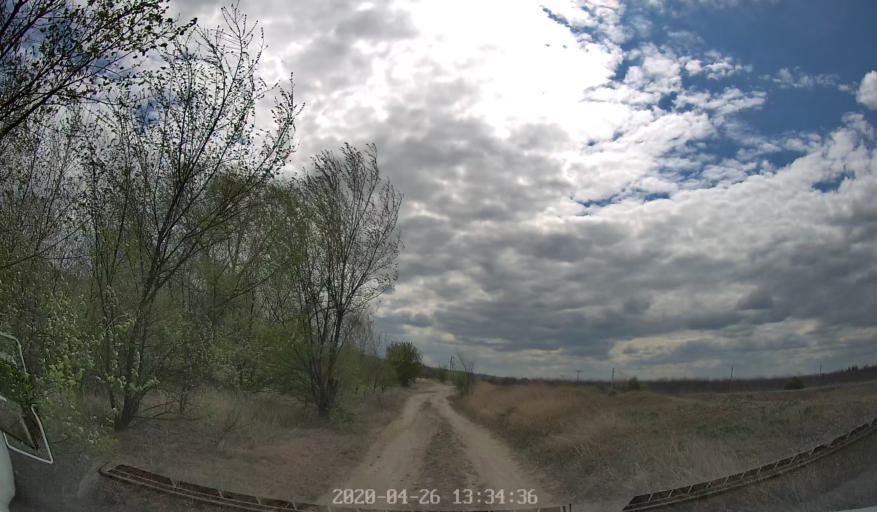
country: MD
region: Criuleni
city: Criuleni
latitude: 47.2062
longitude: 29.1772
